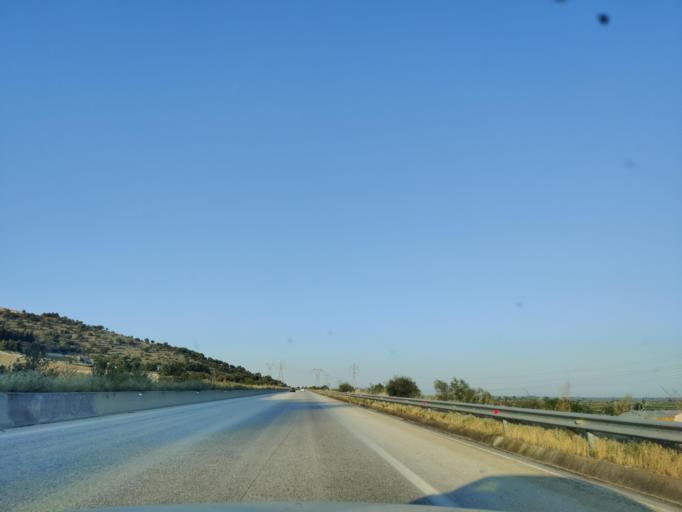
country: GR
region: East Macedonia and Thrace
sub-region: Nomos Kavalas
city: Nea Karvali
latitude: 40.9716
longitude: 24.5504
